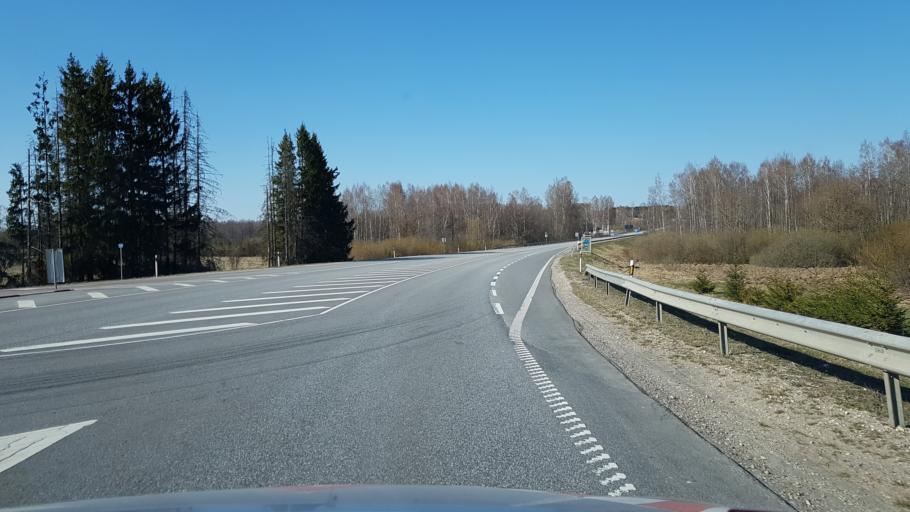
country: EE
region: Tartu
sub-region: Tartu linn
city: Tartu
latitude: 58.4621
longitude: 26.7860
